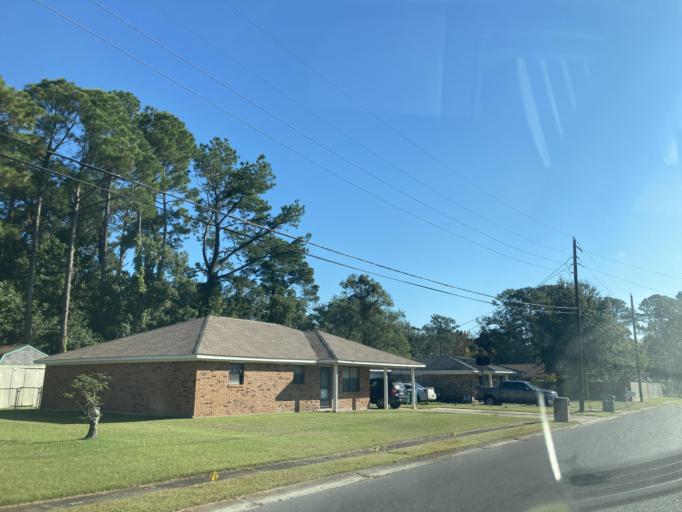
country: US
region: Mississippi
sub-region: Jackson County
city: Saint Martin
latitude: 30.4463
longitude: -88.8827
